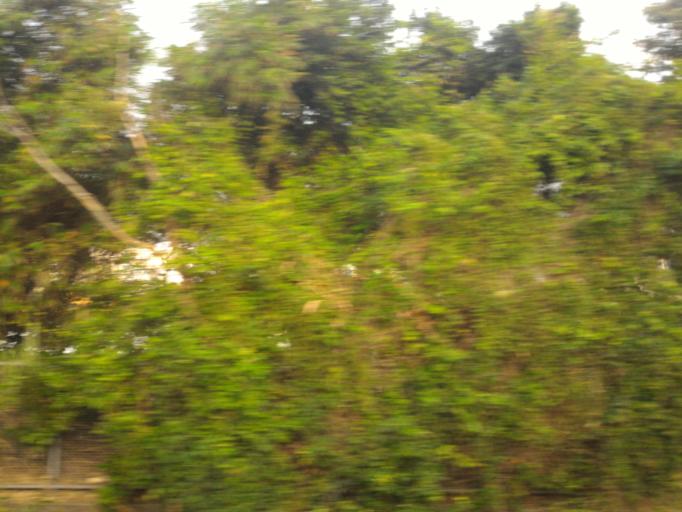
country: TW
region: Taiwan
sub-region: Taoyuan
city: Taoyuan
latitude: 24.9607
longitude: 121.3389
